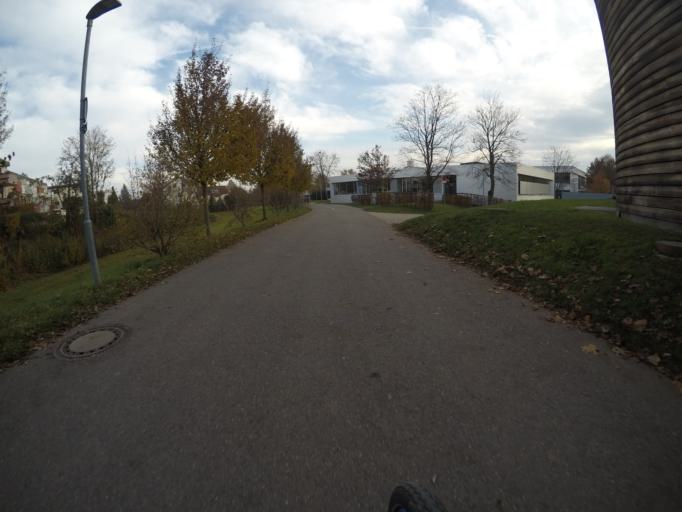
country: DE
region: Baden-Wuerttemberg
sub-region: Regierungsbezirk Stuttgart
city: Leinfelden-Echterdingen
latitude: 48.6900
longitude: 9.1544
